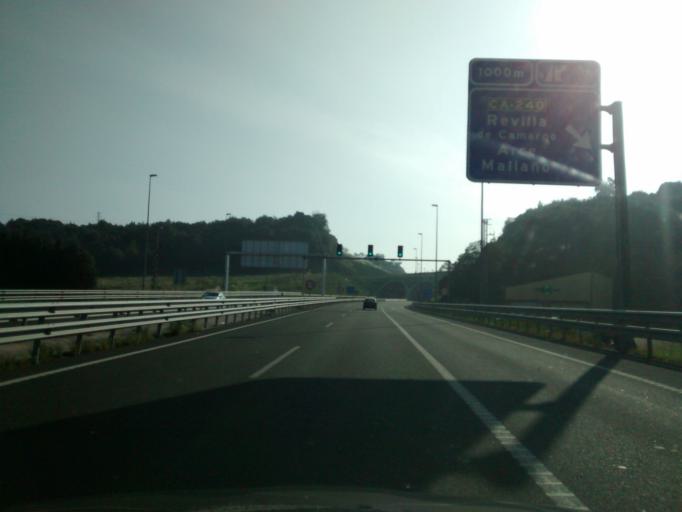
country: ES
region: Cantabria
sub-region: Provincia de Cantabria
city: Camargo
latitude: 43.4170
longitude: -3.8720
